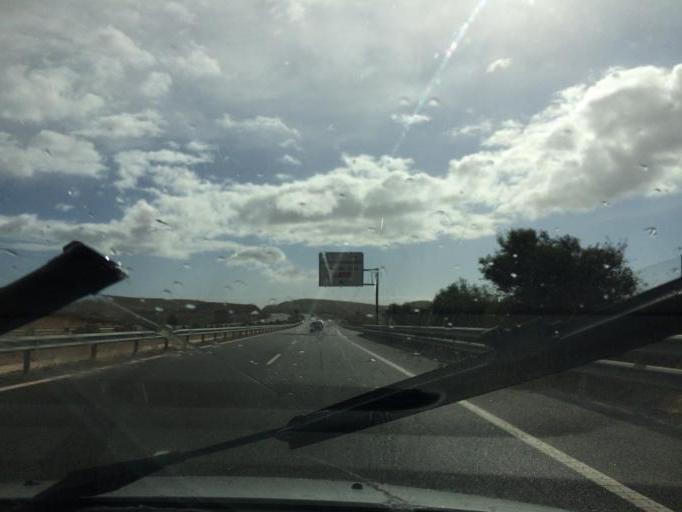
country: ES
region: Andalusia
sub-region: Provincia de Almeria
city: Retamar
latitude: 36.8674
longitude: -2.2729
